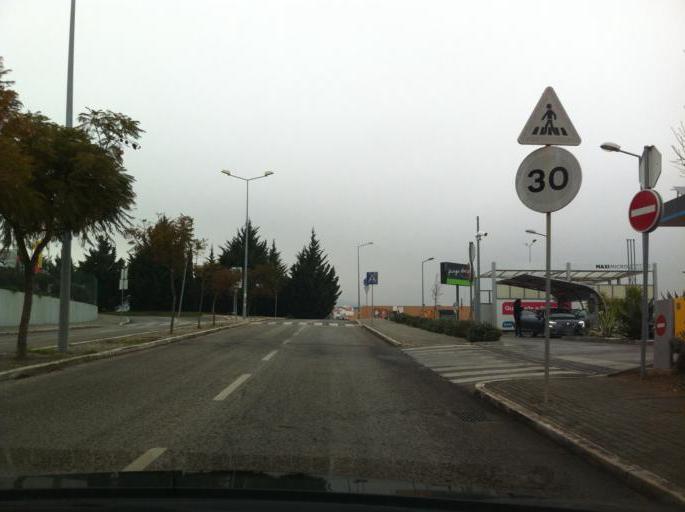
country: PT
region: Lisbon
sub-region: Odivelas
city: Famoes
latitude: 38.7900
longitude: -9.2148
